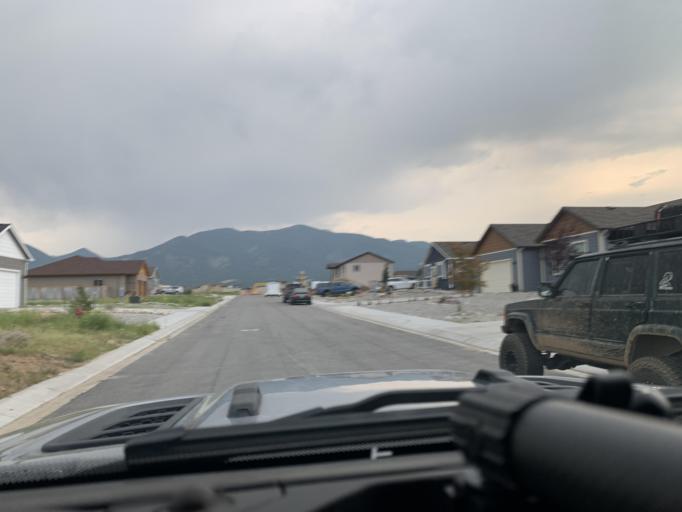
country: US
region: Colorado
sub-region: Chaffee County
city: Buena Vista
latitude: 38.8305
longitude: -106.1516
